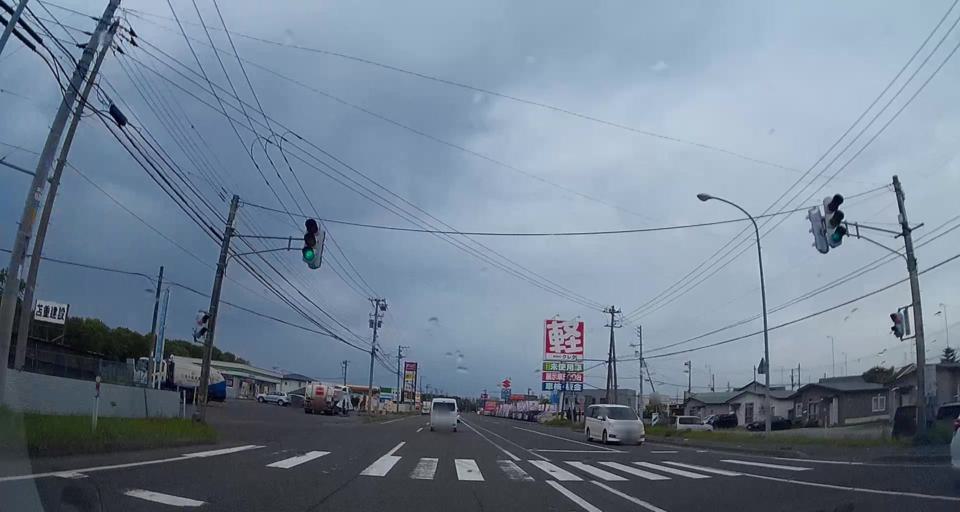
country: JP
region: Hokkaido
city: Tomakomai
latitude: 42.6734
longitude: 141.7060
